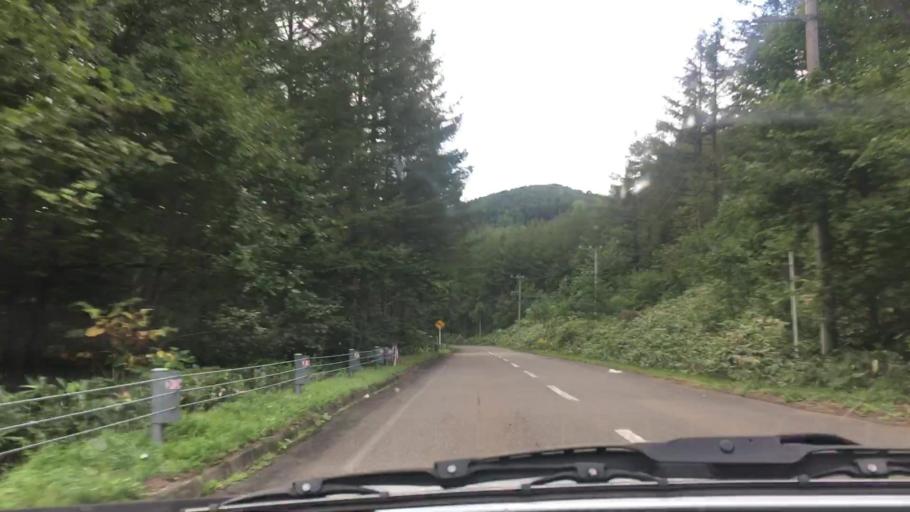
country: JP
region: Hokkaido
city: Otofuke
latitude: 43.1539
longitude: 142.8581
